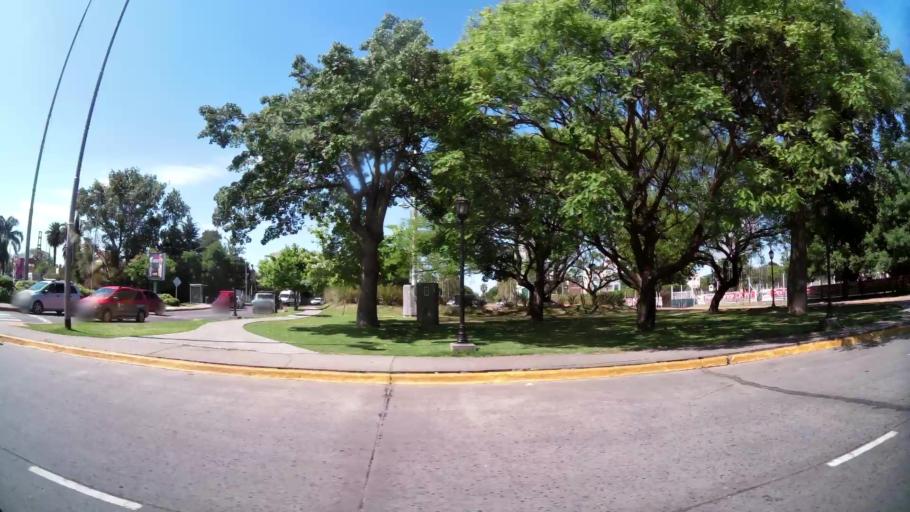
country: AR
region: Buenos Aires
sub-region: Partido de Tigre
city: Tigre
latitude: -34.4274
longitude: -58.5839
